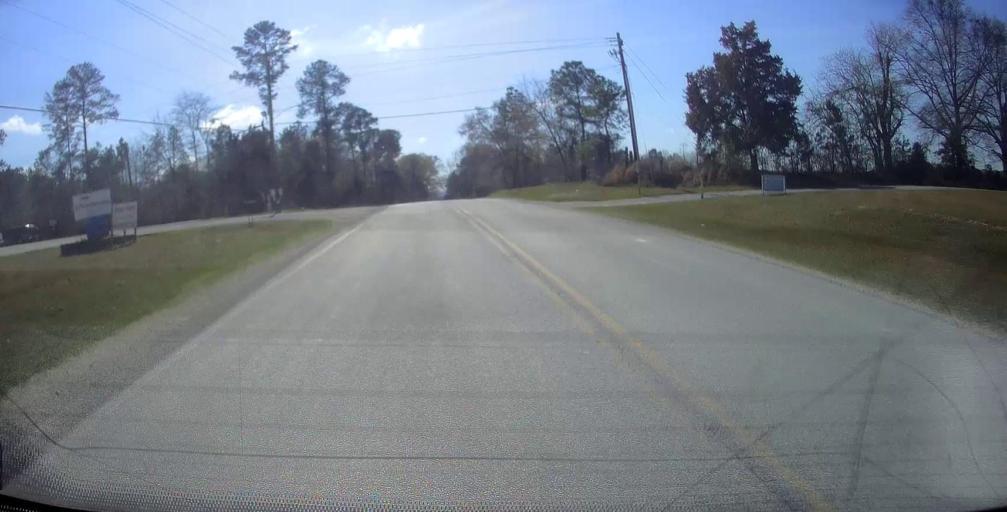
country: US
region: Georgia
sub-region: Wilkinson County
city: Gordon
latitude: 32.8923
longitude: -83.3111
